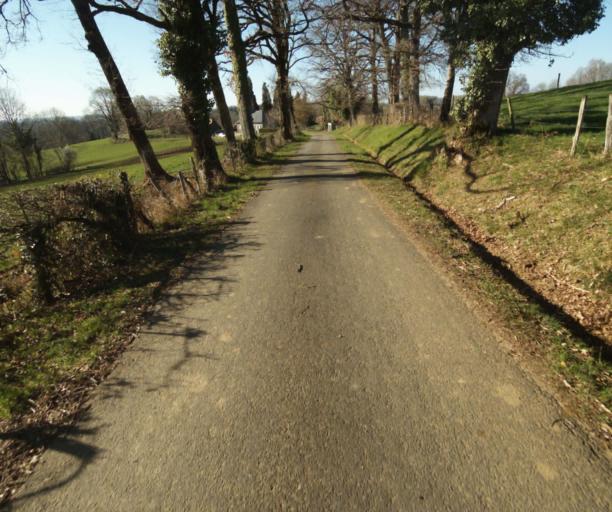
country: FR
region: Limousin
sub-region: Departement de la Correze
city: Seilhac
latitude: 45.3870
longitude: 1.6761
